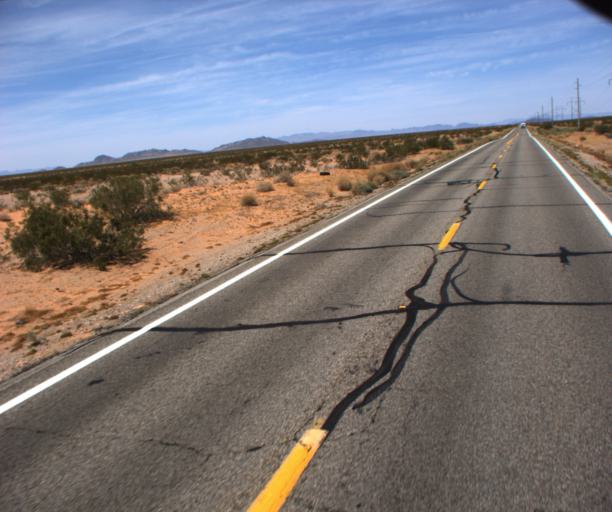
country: US
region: Arizona
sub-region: La Paz County
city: Quartzsite
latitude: 33.8621
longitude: -114.2169
